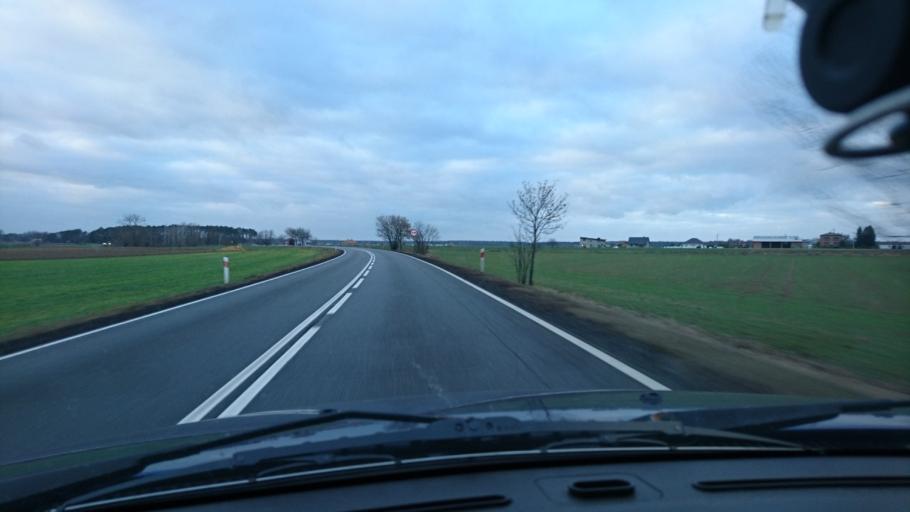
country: PL
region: Greater Poland Voivodeship
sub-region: Powiat kepinski
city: Opatow
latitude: 51.2188
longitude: 18.1379
